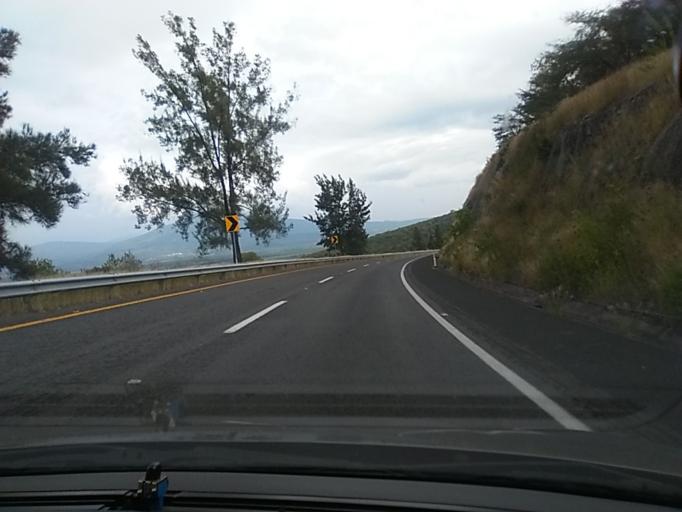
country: MX
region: Michoacan
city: Ixtlan
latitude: 20.1997
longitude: -102.3214
